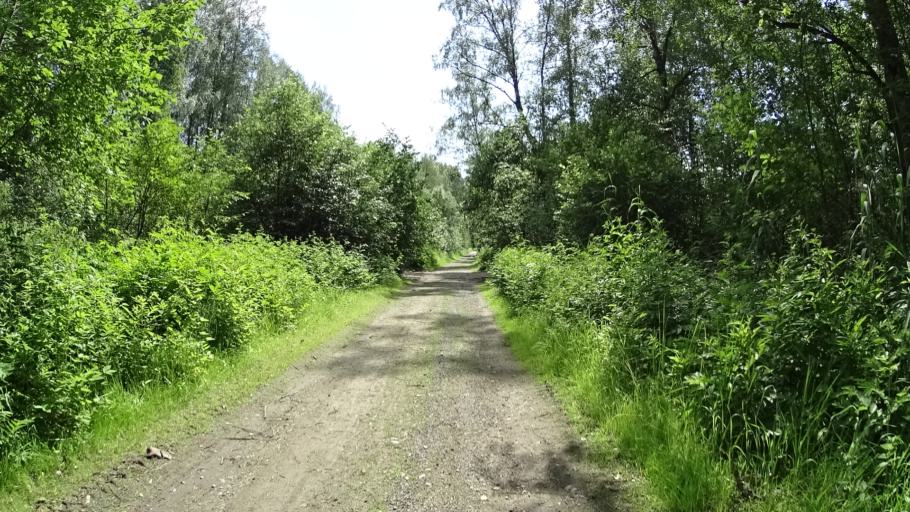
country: FI
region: Uusimaa
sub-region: Raaseporin
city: Pohja
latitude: 60.1064
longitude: 23.5485
